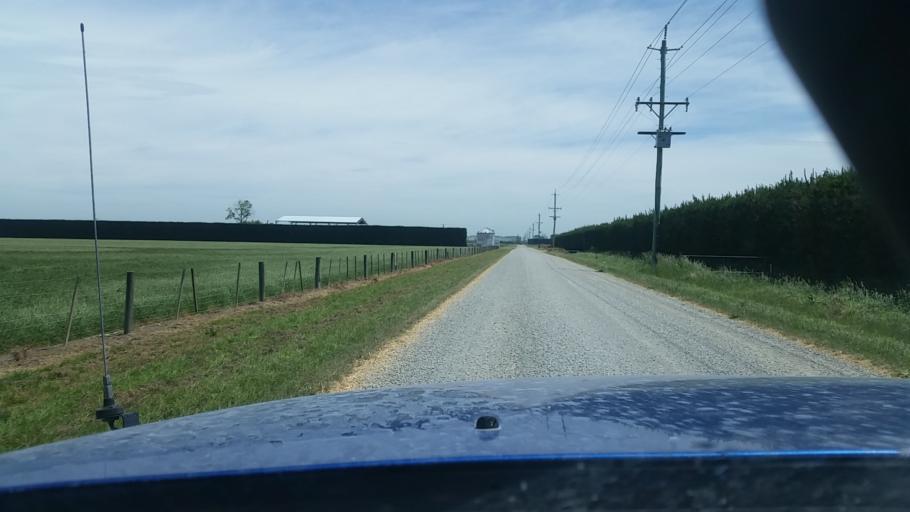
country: NZ
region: Canterbury
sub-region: Ashburton District
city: Tinwald
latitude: -44.0097
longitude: 171.7536
